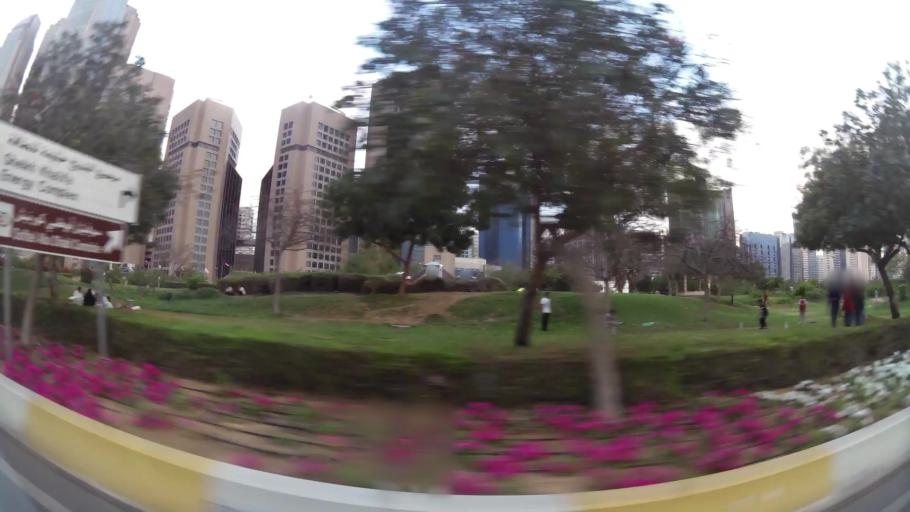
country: AE
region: Abu Dhabi
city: Abu Dhabi
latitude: 24.4993
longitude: 54.3648
